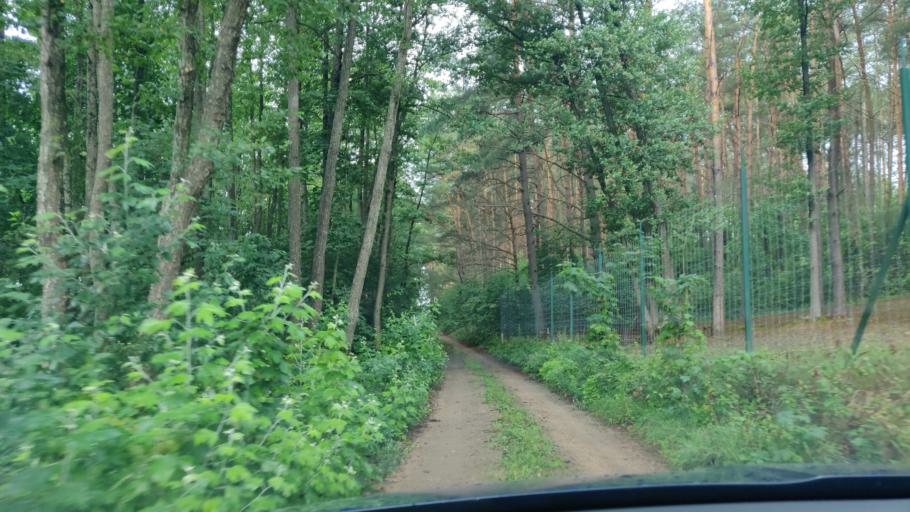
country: LT
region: Vilnius County
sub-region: Trakai
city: Rudiskes
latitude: 54.6097
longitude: 24.8311
